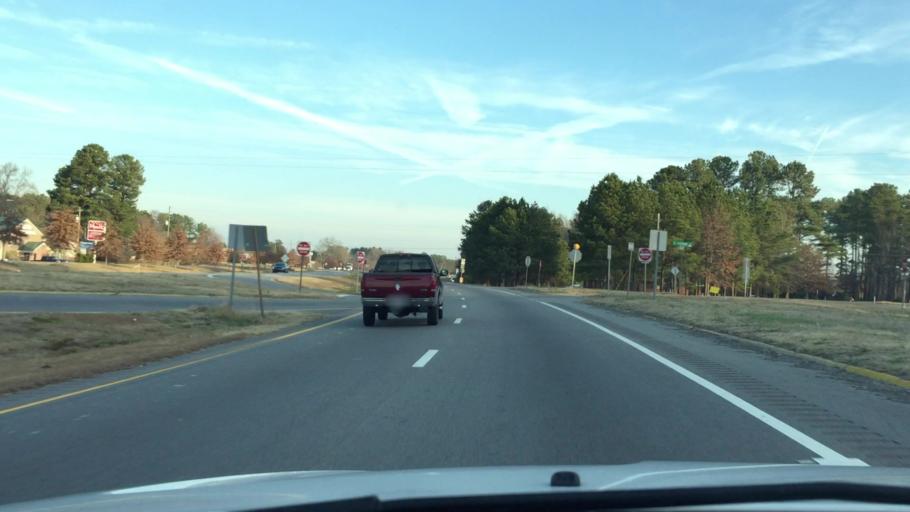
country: US
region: North Carolina
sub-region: Lee County
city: Sanford
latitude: 35.4439
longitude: -79.2149
